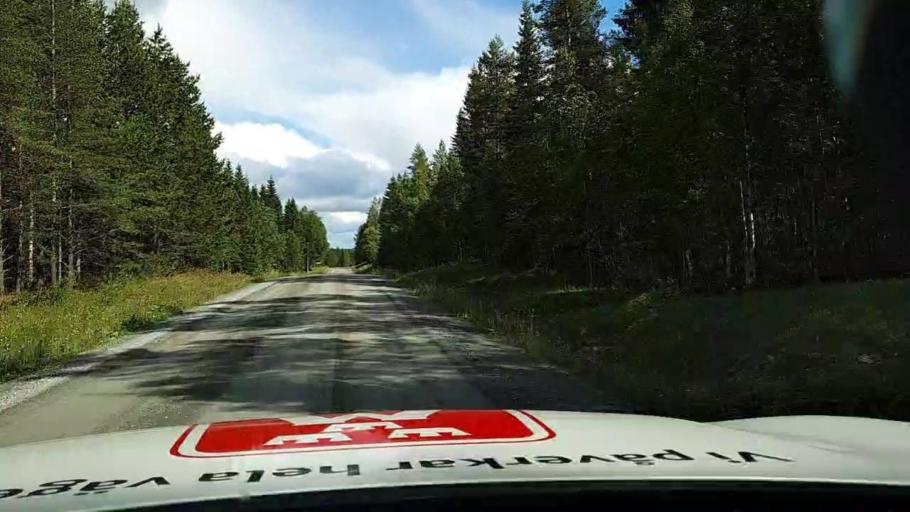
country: SE
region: Jaemtland
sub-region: Krokoms Kommun
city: Valla
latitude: 63.6679
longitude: 13.7070
